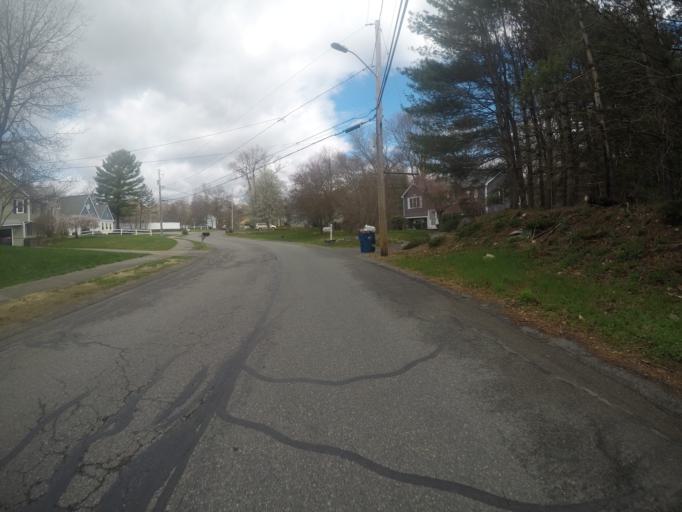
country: US
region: Massachusetts
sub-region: Bristol County
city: Easton
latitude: 42.0265
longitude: -71.1545
